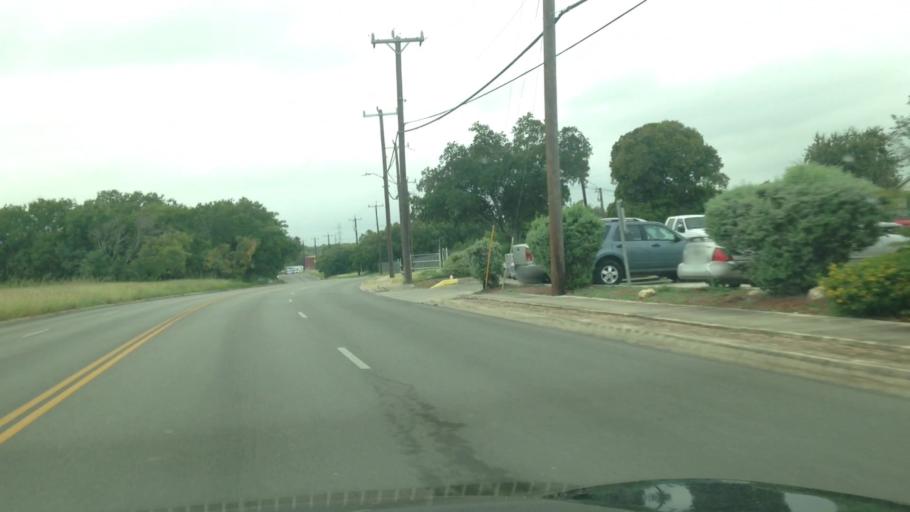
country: US
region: Texas
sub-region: Bexar County
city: Live Oak
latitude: 29.5830
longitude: -98.3954
